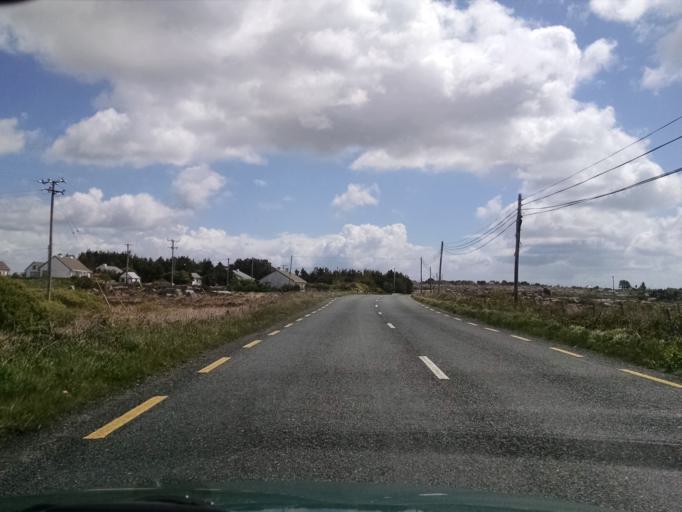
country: IE
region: Connaught
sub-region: County Galway
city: Oughterard
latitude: 53.3129
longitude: -9.6079
